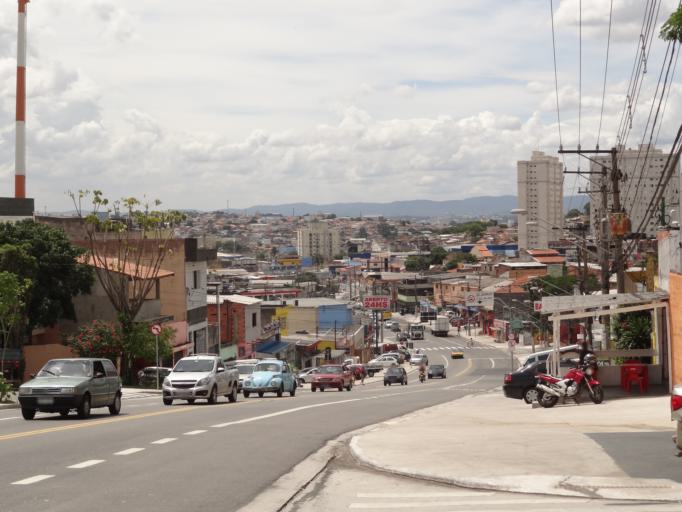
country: BR
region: Sao Paulo
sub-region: Ferraz De Vasconcelos
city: Ferraz de Vasconcelos
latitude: -23.5177
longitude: -46.4218
